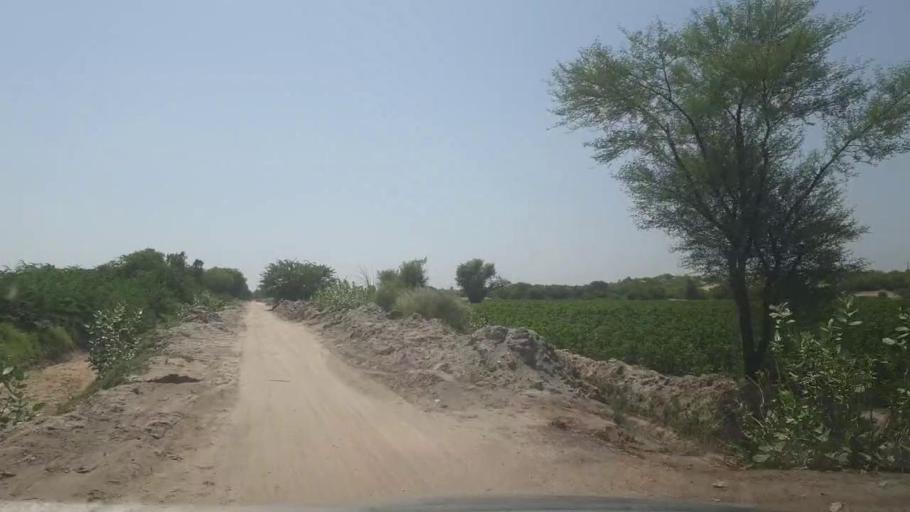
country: PK
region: Sindh
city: Khairpur
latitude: 27.3544
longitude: 69.0419
